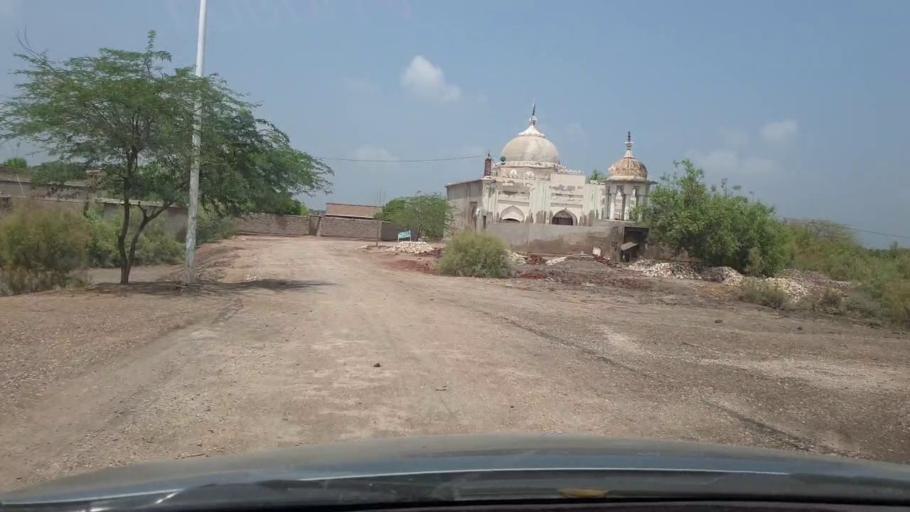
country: PK
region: Sindh
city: Khairpur
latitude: 27.4783
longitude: 68.6933
